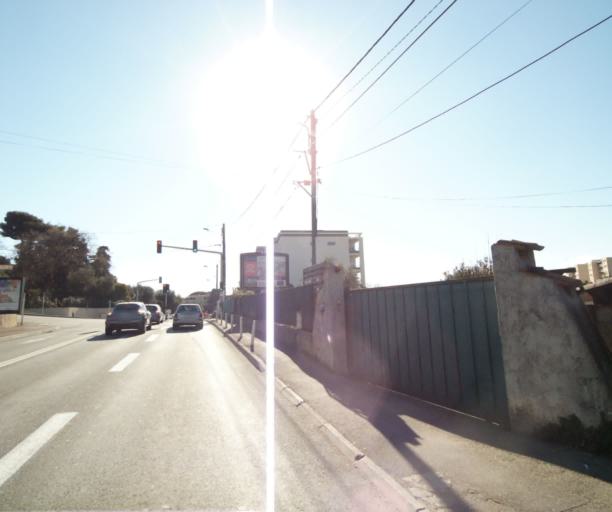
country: FR
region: Provence-Alpes-Cote d'Azur
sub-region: Departement des Alpes-Maritimes
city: Biot
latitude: 43.5965
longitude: 7.1055
